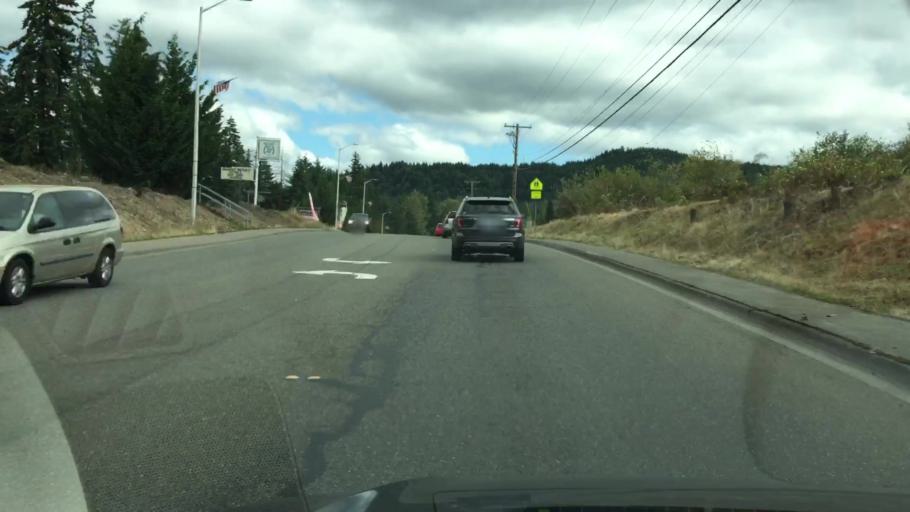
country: US
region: Washington
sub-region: Pierce County
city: Eatonville
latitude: 46.8647
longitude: -122.2587
